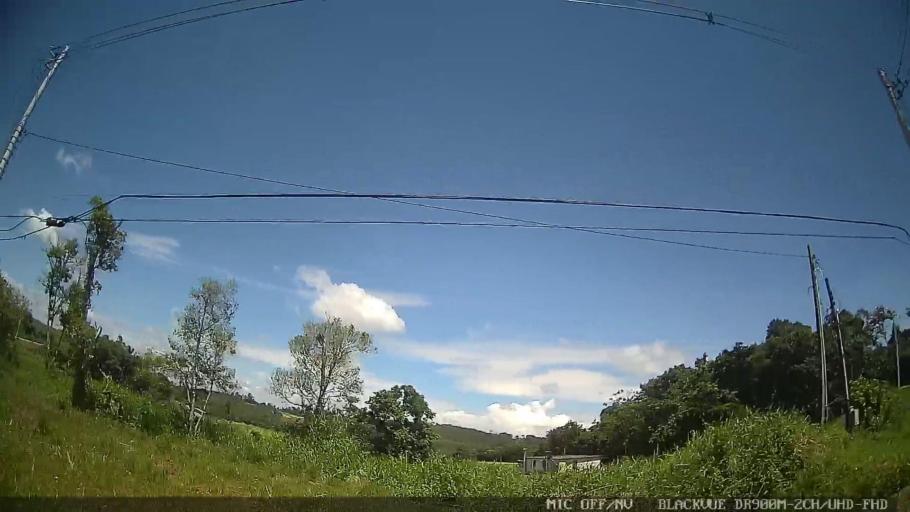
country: BR
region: Sao Paulo
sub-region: Biritiba-Mirim
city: Biritiba Mirim
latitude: -23.5772
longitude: -46.0794
